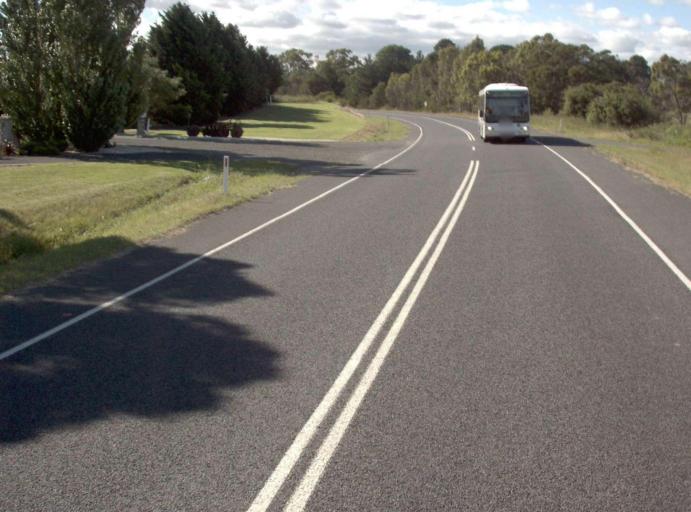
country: AU
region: Victoria
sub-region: Latrobe
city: Traralgon
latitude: -38.1677
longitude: 146.4901
